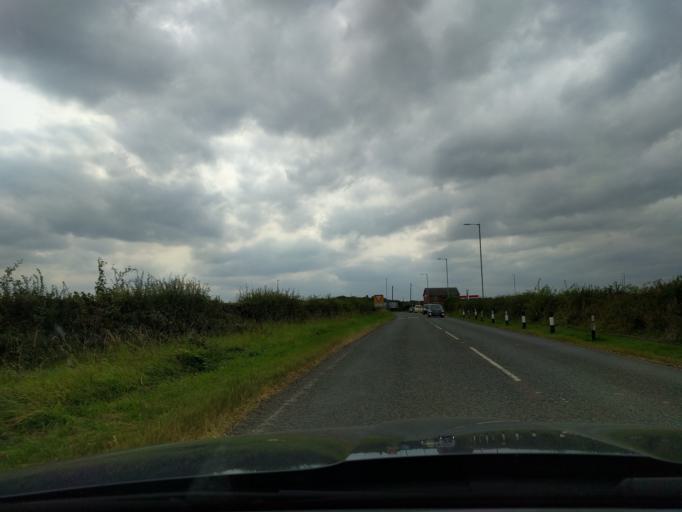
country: GB
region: England
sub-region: Northumberland
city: Stannington
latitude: 55.1283
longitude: -1.6405
